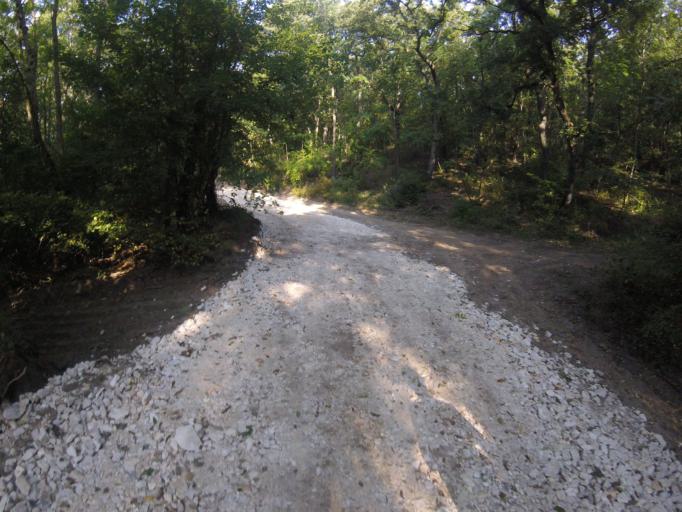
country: HU
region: Komarom-Esztergom
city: Piliscsev
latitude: 47.6922
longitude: 18.8469
